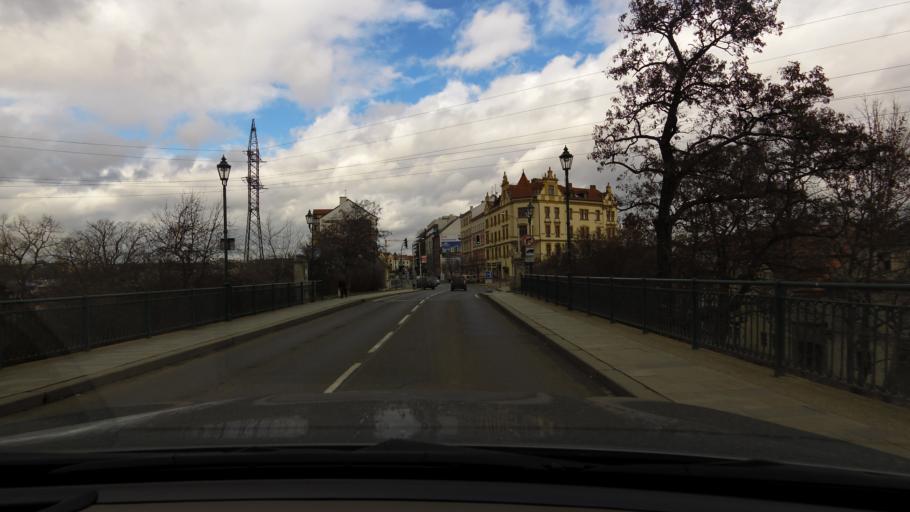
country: CZ
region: Plzensky
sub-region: Okres Plzen-Mesto
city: Pilsen
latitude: 49.7513
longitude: 13.3792
